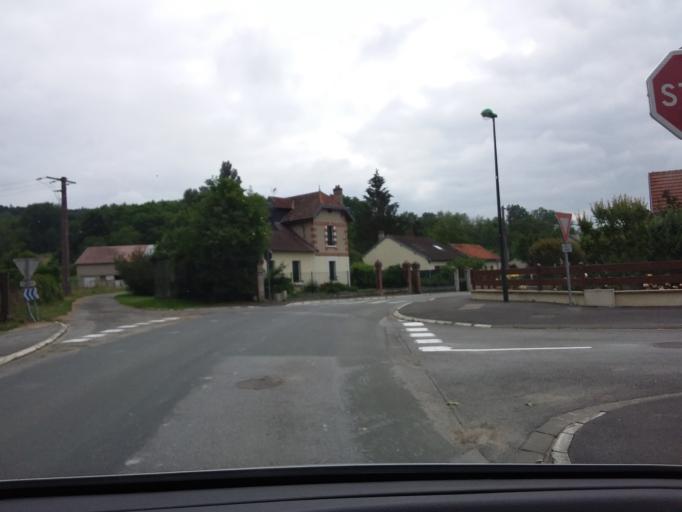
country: FR
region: Picardie
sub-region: Departement de l'Aisne
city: Vailly-sur-Aisne
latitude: 49.4086
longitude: 3.5255
